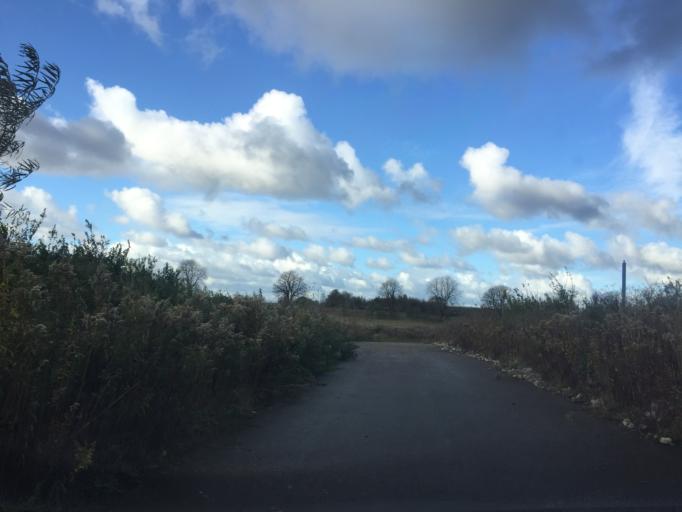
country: DK
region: Capital Region
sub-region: Hoje-Taastrup Kommune
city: Taastrup
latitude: 55.6572
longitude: 12.2654
